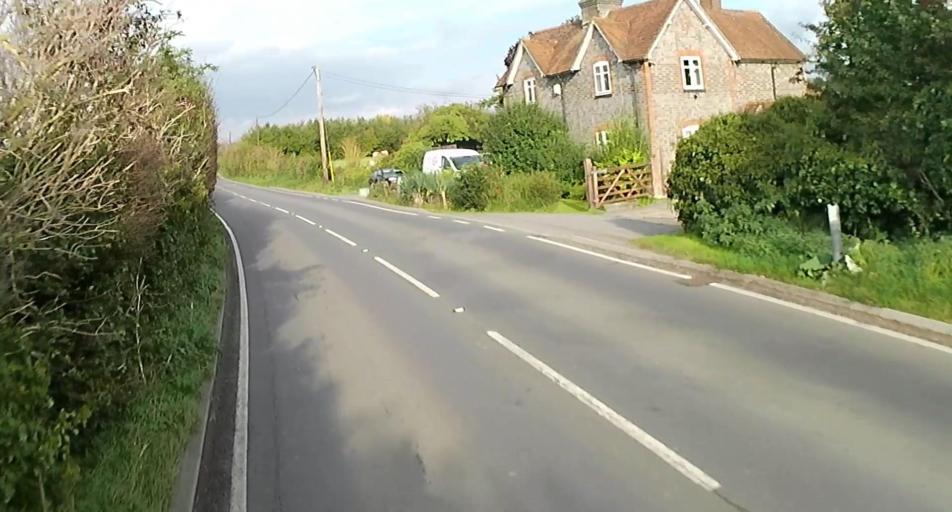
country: GB
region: England
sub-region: West Berkshire
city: Thatcham
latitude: 51.3878
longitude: -1.2474
